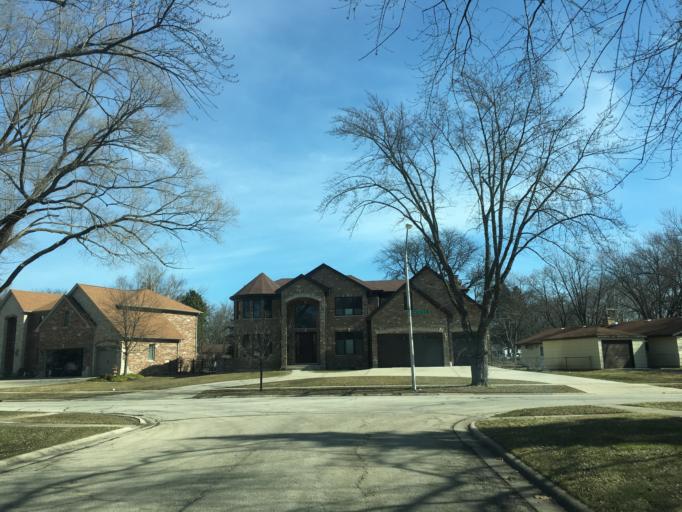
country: US
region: Illinois
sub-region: DuPage County
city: Hanover Park
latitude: 42.0238
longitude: -88.1238
